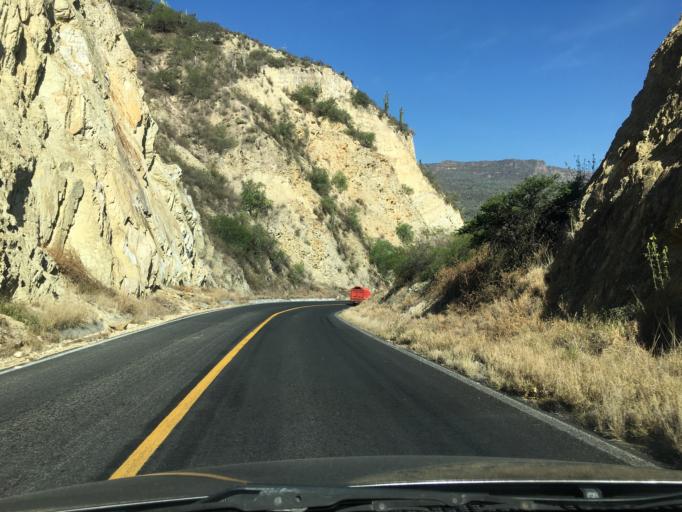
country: MX
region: Hidalgo
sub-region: San Agustin Metzquititlan
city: Mezquititlan
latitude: 20.4667
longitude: -98.6755
